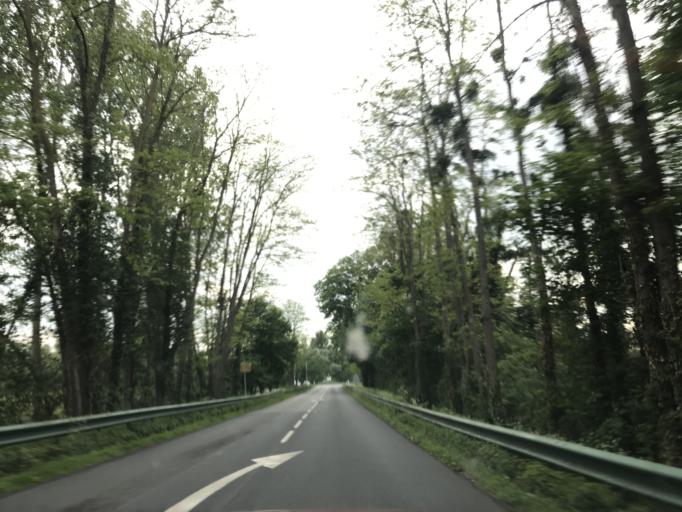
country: FR
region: Auvergne
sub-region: Departement du Puy-de-Dome
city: Maringues
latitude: 45.9162
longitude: 3.3688
